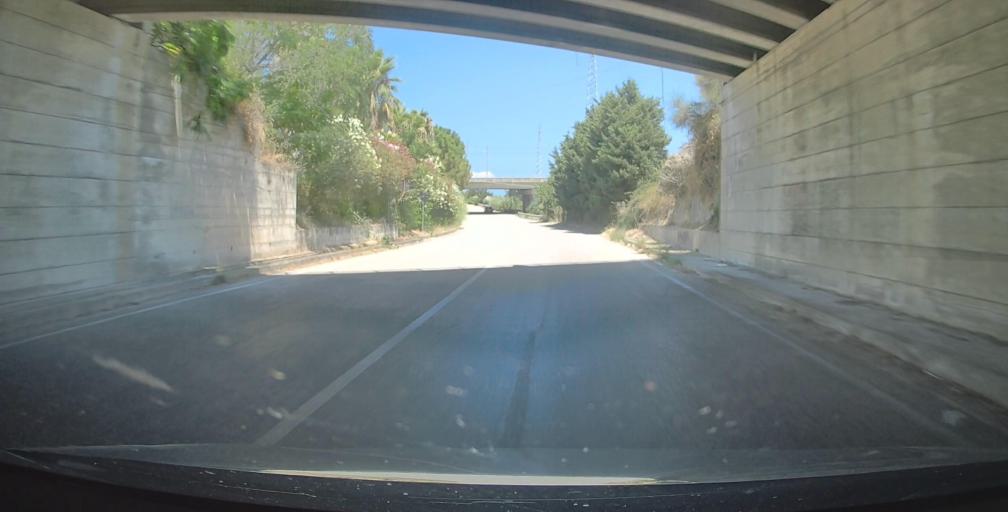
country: IT
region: Sicily
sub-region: Messina
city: Patti
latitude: 38.1388
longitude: 14.9970
